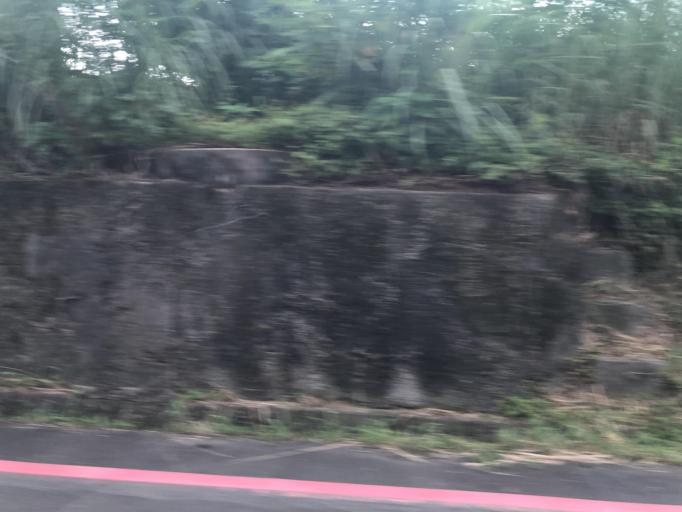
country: TW
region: Taiwan
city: Daxi
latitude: 24.9213
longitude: 121.3600
